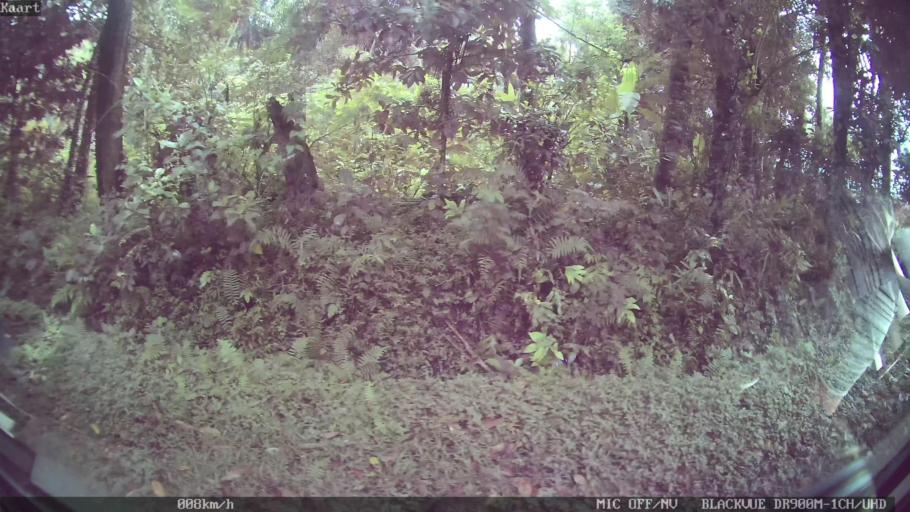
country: ID
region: Bali
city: Bunutan
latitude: -8.4684
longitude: 115.2348
